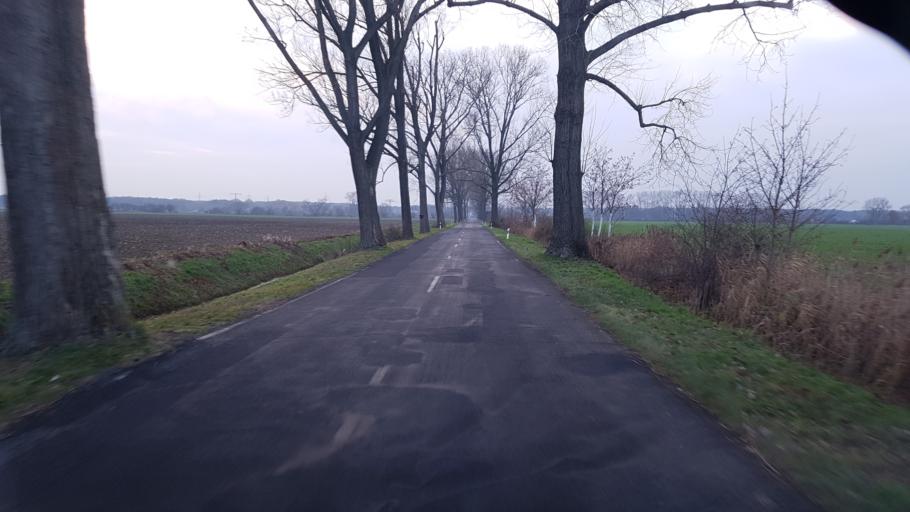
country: DE
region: Brandenburg
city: Ziltendorf
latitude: 52.2143
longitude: 14.6452
